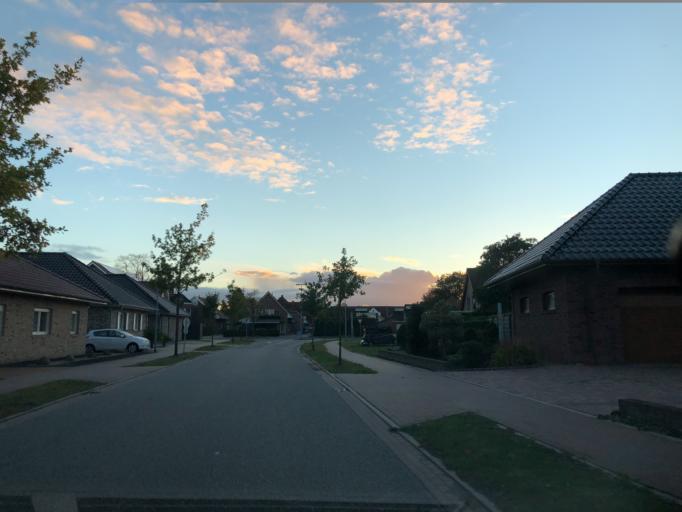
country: DE
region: Lower Saxony
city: Papenburg
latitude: 53.0855
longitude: 7.4105
